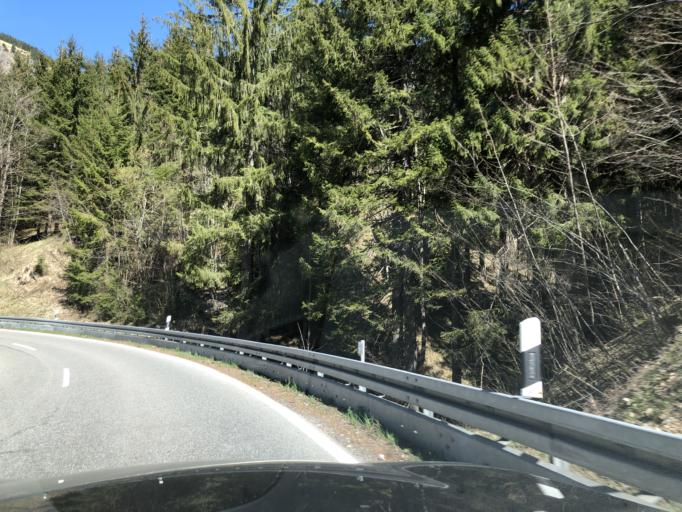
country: AT
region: Tyrol
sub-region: Politischer Bezirk Reutte
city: Schattwald
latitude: 47.5086
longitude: 10.3862
